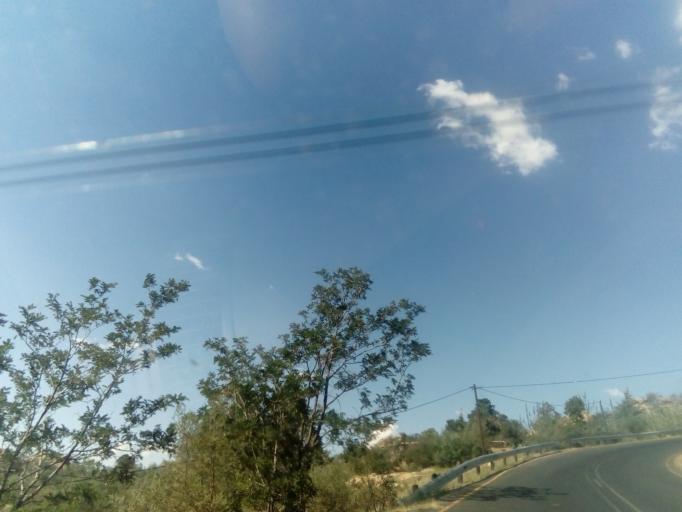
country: LS
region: Berea
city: Teyateyaneng
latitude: -29.1141
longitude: 27.8209
